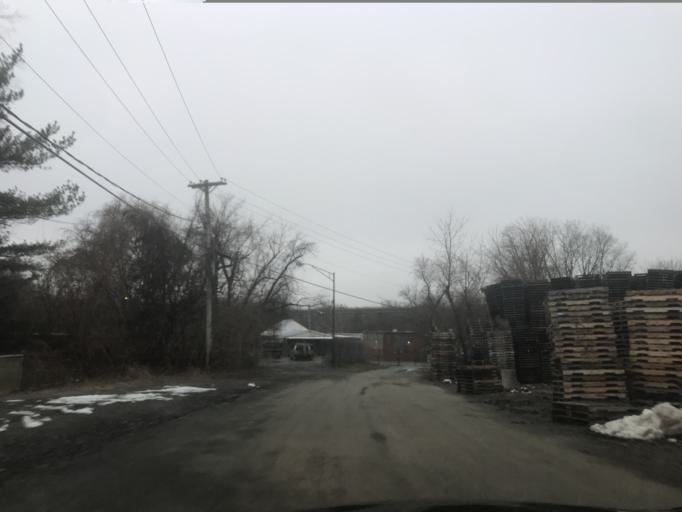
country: US
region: Maryland
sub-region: Baltimore County
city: Rossville
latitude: 39.3255
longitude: -76.4748
